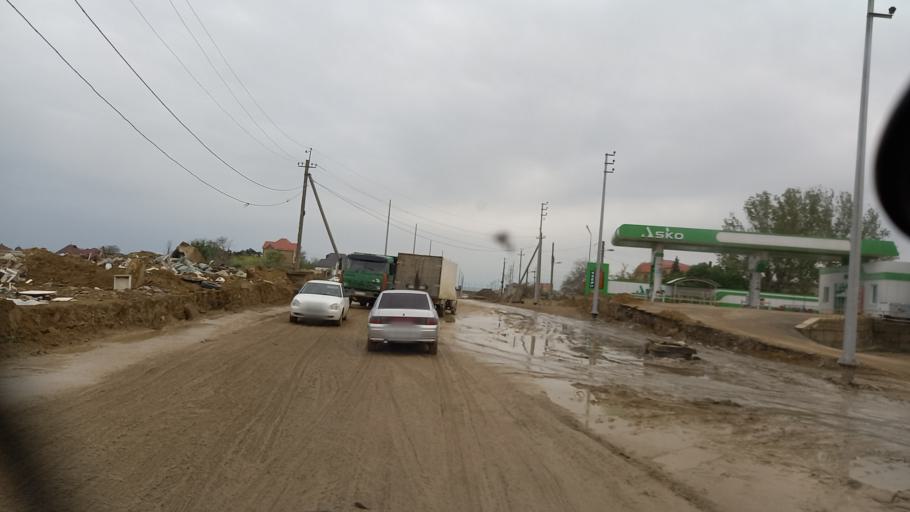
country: RU
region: Dagestan
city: Derbent
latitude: 42.0999
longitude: 48.2852
